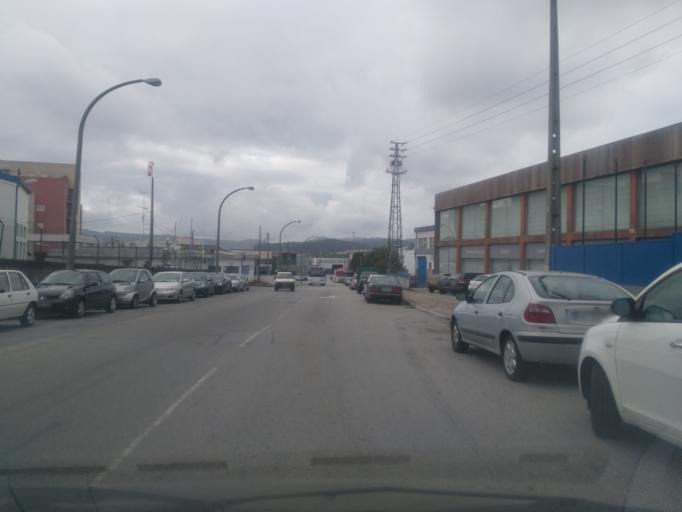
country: PT
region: Braga
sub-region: Braga
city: Braga
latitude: 41.5406
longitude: -8.4356
